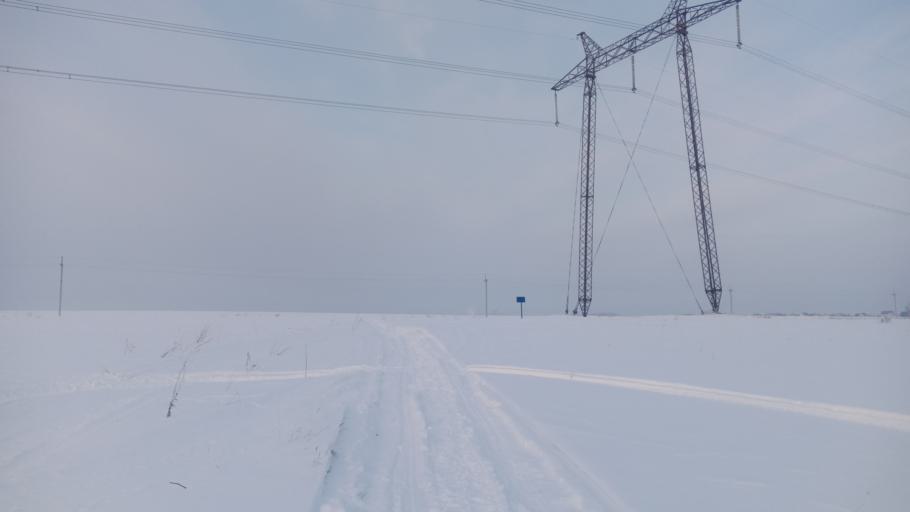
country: RU
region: Altai Krai
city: Nauchnyy Gorodok
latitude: 53.4050
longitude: 83.5140
